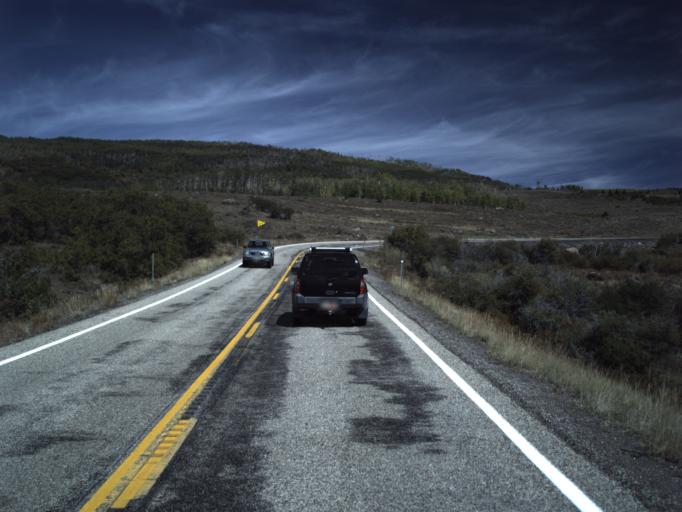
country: US
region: Utah
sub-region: Wayne County
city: Loa
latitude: 38.0080
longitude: -111.3897
